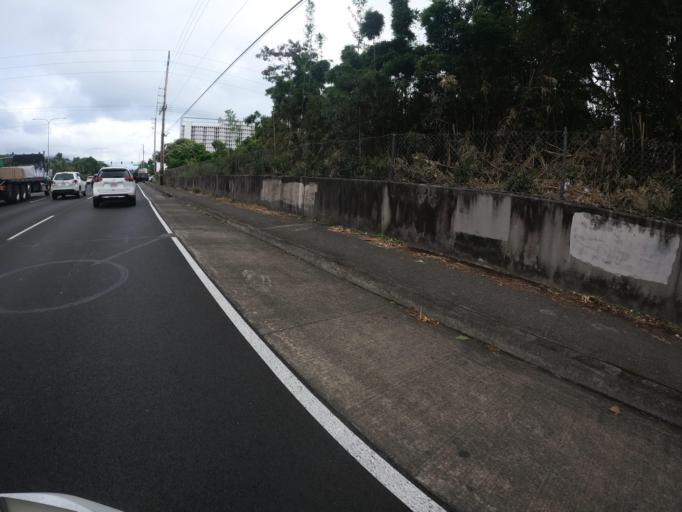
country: US
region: Hawaii
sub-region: Honolulu County
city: Kane'ohe
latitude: 21.4128
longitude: -157.8097
